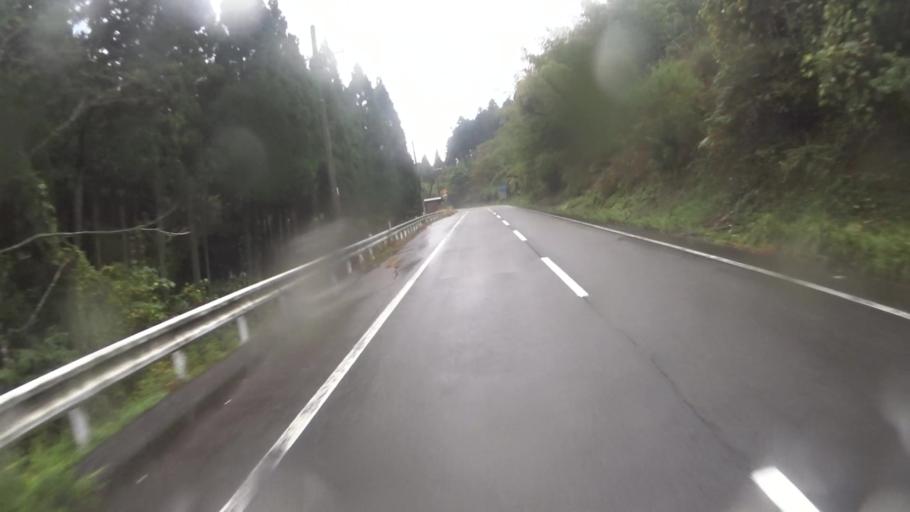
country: JP
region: Kyoto
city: Miyazu
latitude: 35.5096
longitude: 135.2409
